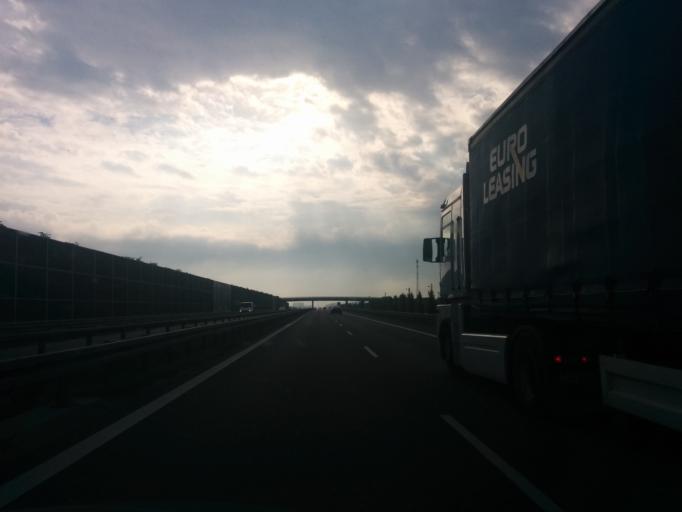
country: PL
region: Masovian Voivodeship
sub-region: Powiat radomski
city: Jedlinsk
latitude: 51.5463
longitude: 21.0520
